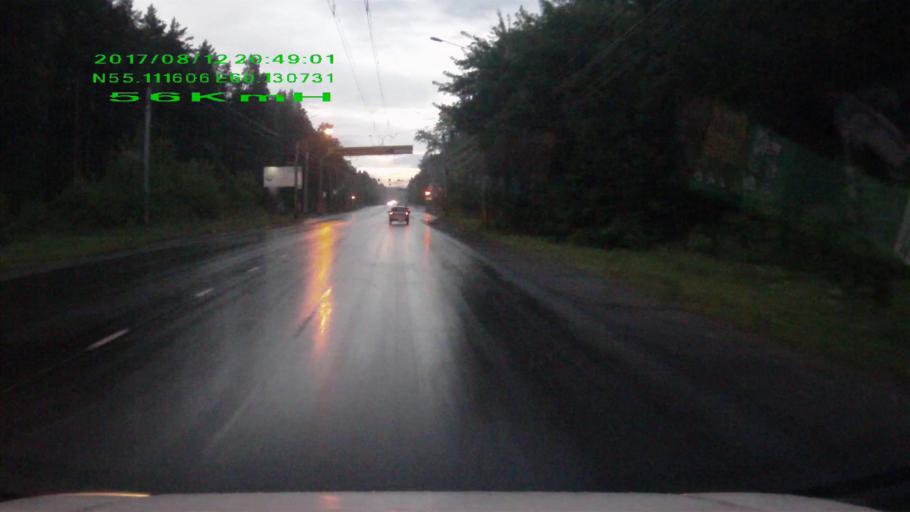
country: RU
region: Chelyabinsk
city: Turgoyak
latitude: 55.1118
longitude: 60.1307
